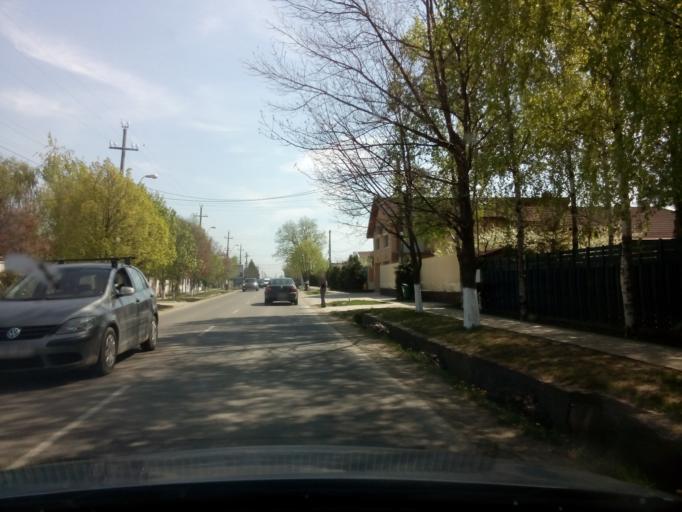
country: RO
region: Ilfov
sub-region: Comuna Corbeanca
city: Corbeanca
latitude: 44.5964
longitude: 26.0517
